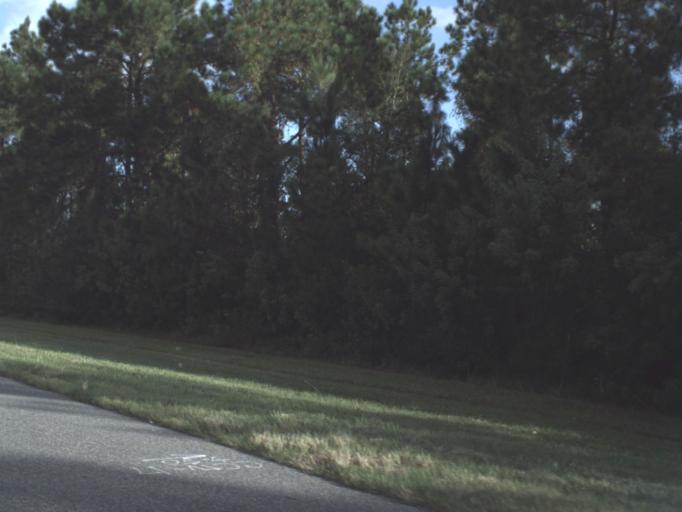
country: US
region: Florida
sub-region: Orange County
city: Taft
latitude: 28.4221
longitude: -81.3942
